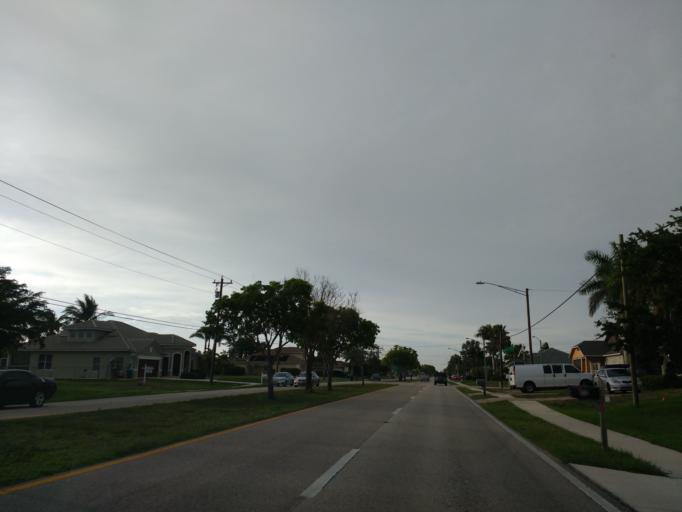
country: US
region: Florida
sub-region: Lee County
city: Cape Coral
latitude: 26.5759
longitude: -82.0068
